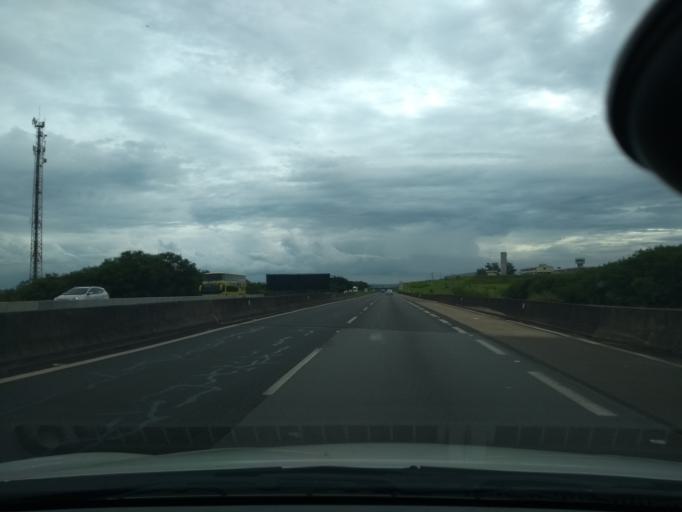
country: BR
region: Sao Paulo
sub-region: Santa Barbara D'Oeste
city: Santa Barbara d'Oeste
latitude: -22.7035
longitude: -47.4561
